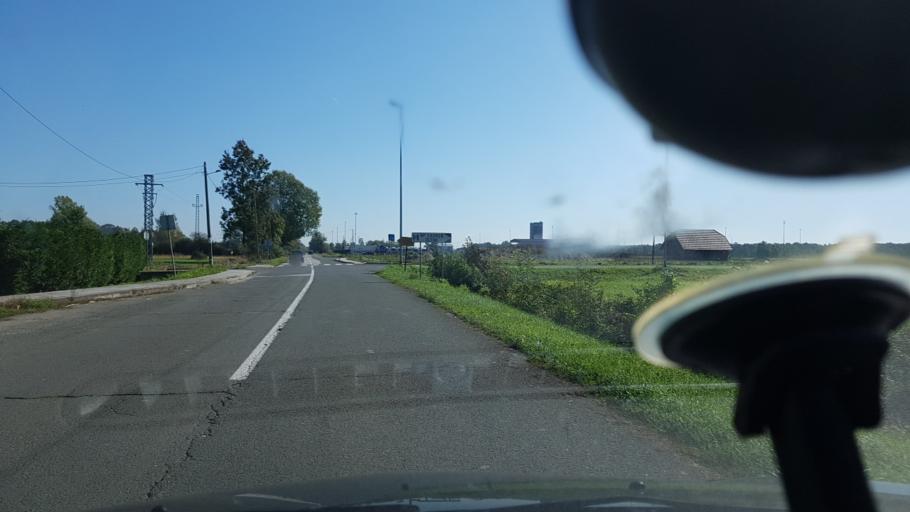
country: HR
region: Zagrebacka
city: Brckovljani
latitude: 45.7575
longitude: 16.2751
